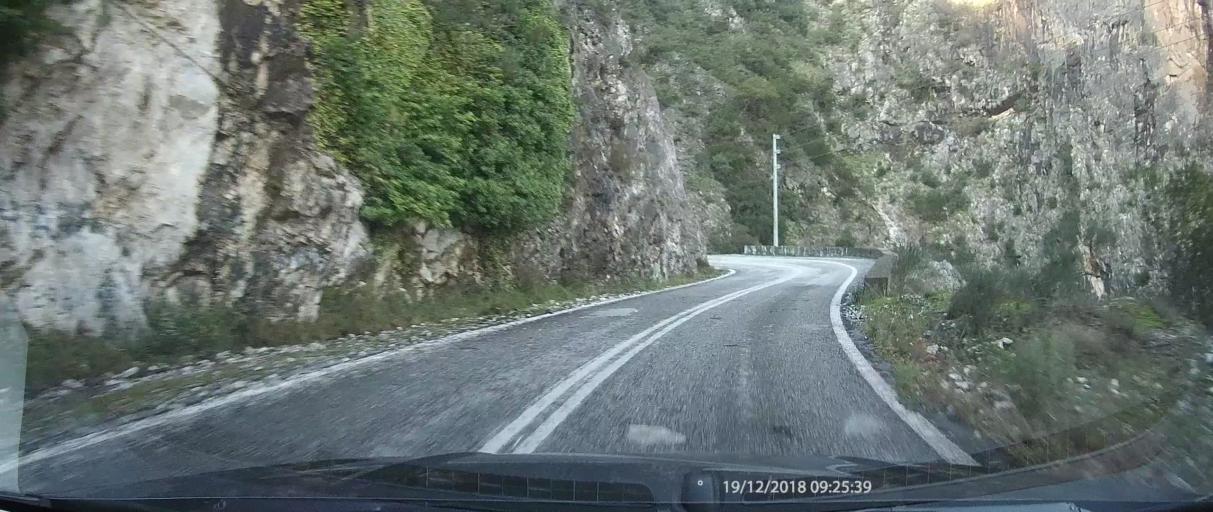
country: GR
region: Peloponnese
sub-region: Nomos Lakonias
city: Magoula
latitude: 37.0956
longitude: 22.3345
